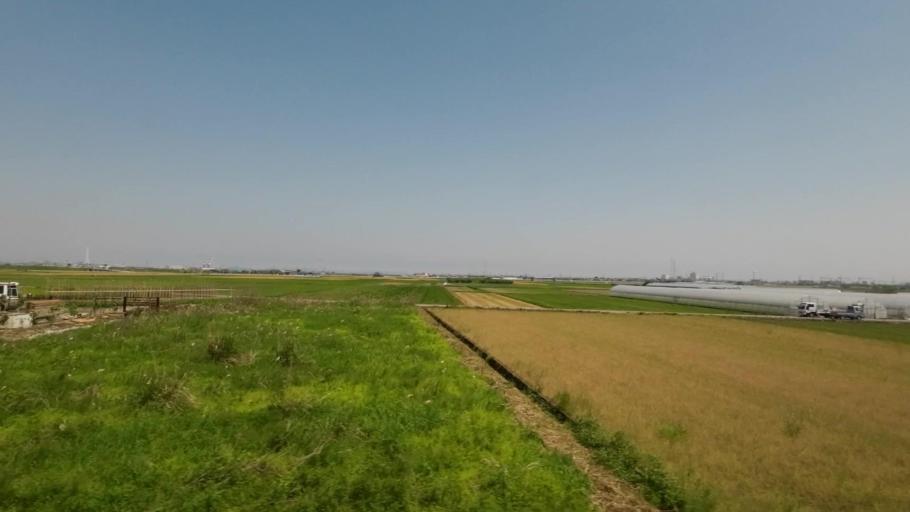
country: JP
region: Ehime
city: Saijo
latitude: 33.8958
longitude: 133.1486
